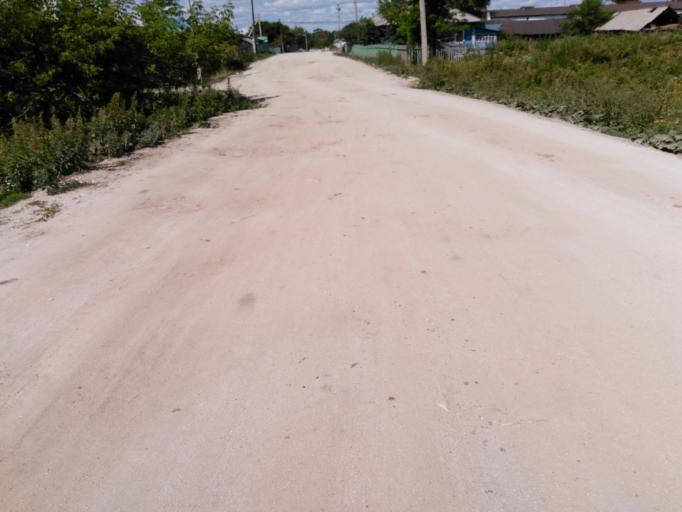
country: RU
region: Bashkortostan
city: Akhunovo
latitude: 54.2087
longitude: 59.6069
